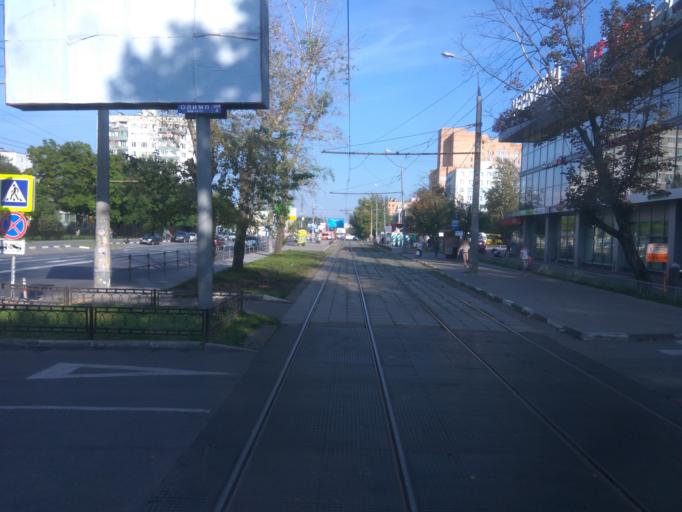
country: RU
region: Moskovskaya
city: Novogireyevo
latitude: 55.7522
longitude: 37.8124
